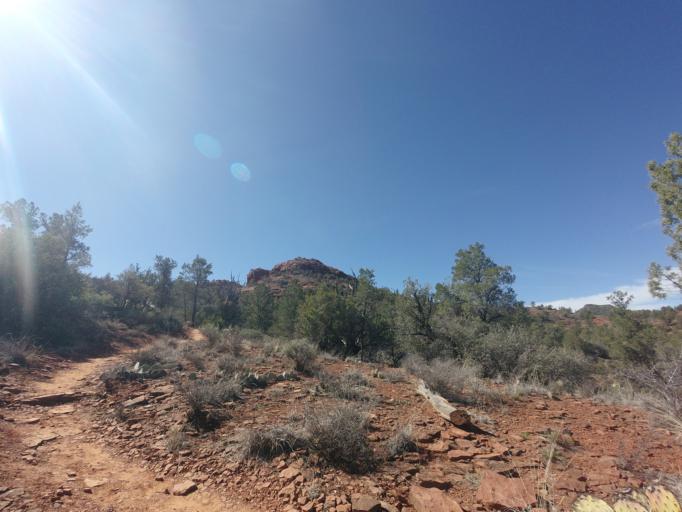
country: US
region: Arizona
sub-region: Yavapai County
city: West Sedona
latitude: 34.8079
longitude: -111.8274
